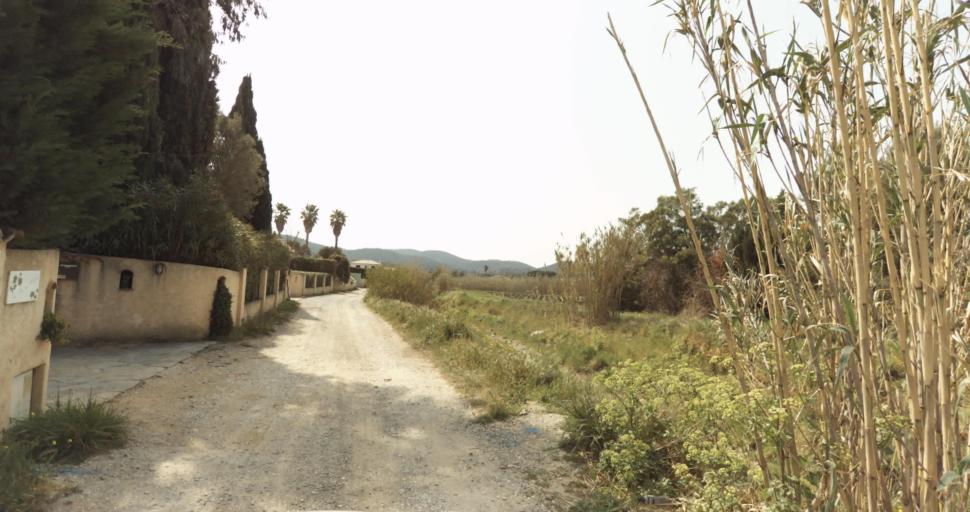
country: FR
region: Provence-Alpes-Cote d'Azur
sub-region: Departement du Var
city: Bormes-les-Mimosas
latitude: 43.1393
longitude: 6.3366
